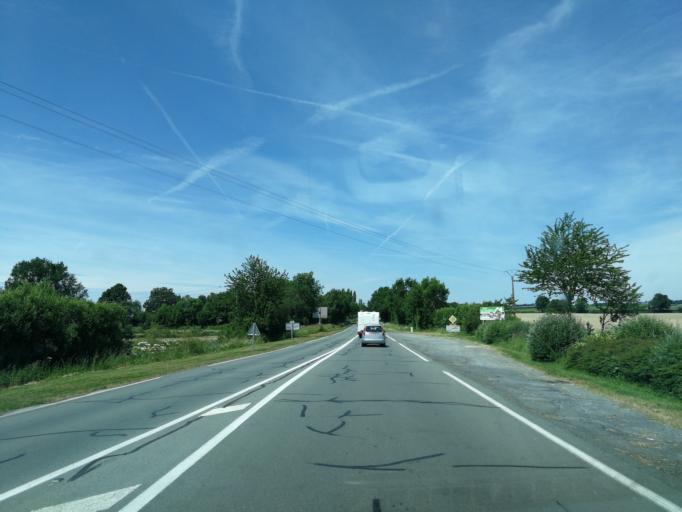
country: FR
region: Pays de la Loire
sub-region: Departement de la Vendee
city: La Tardiere
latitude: 46.6491
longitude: -0.7245
